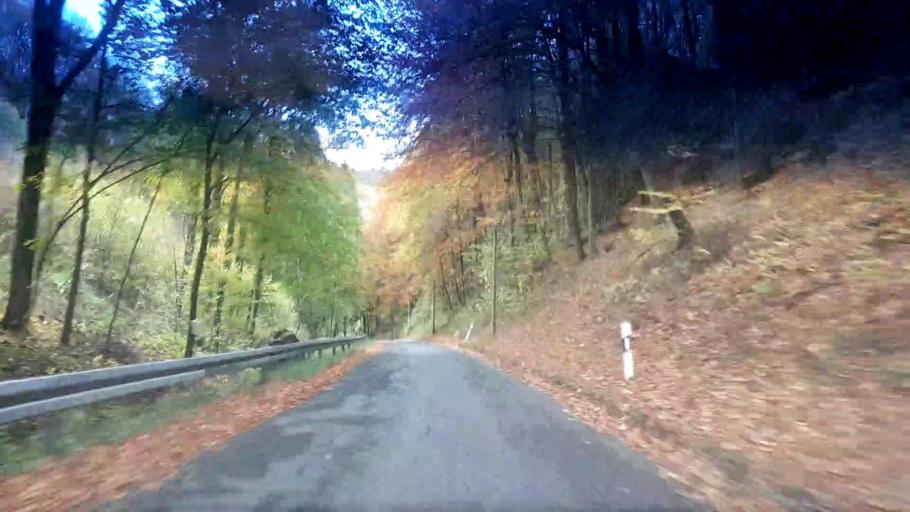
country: DE
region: Bavaria
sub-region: Upper Franconia
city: Wattendorf
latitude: 50.0231
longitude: 11.1046
